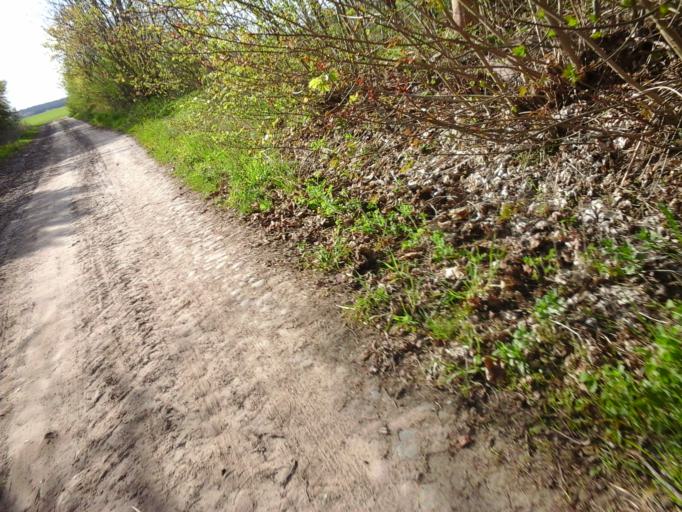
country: PL
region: West Pomeranian Voivodeship
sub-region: Powiat stargardzki
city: Suchan
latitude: 53.2310
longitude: 15.3470
